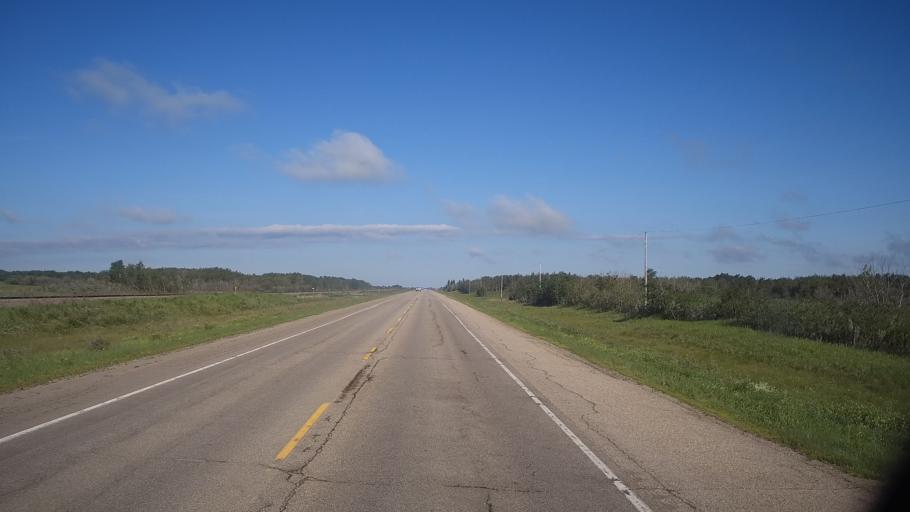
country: CA
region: Saskatchewan
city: Lanigan
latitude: 51.8548
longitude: -105.0847
